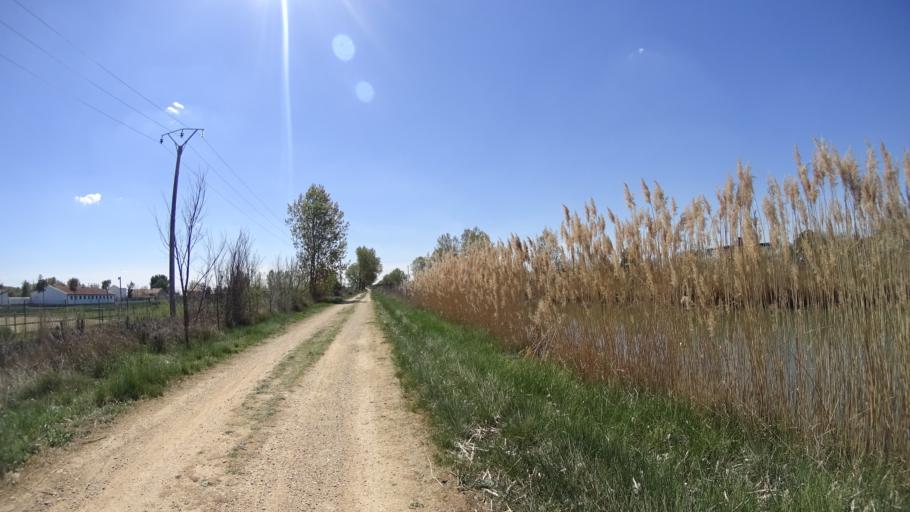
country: ES
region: Castille and Leon
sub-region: Provincia de Valladolid
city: Cabezon
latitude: 41.7437
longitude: -4.6582
